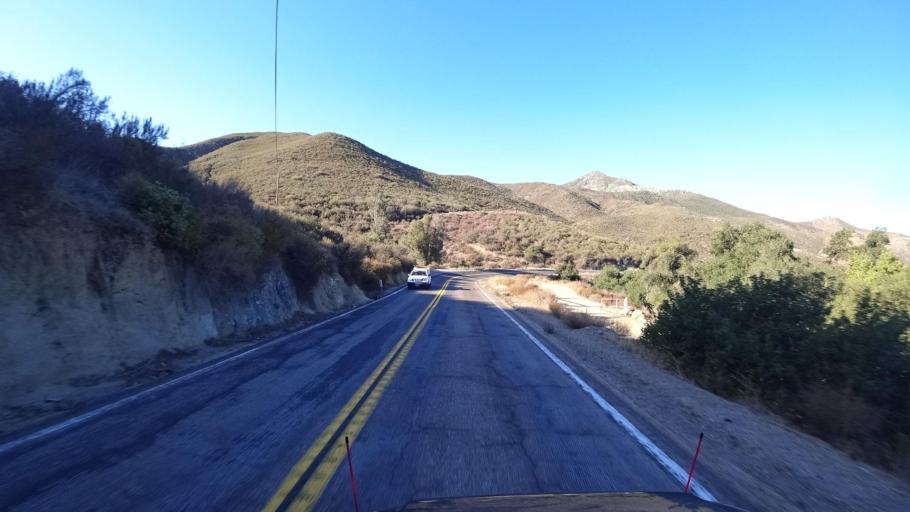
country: MX
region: Baja California
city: Tecate
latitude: 32.5947
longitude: -116.6621
